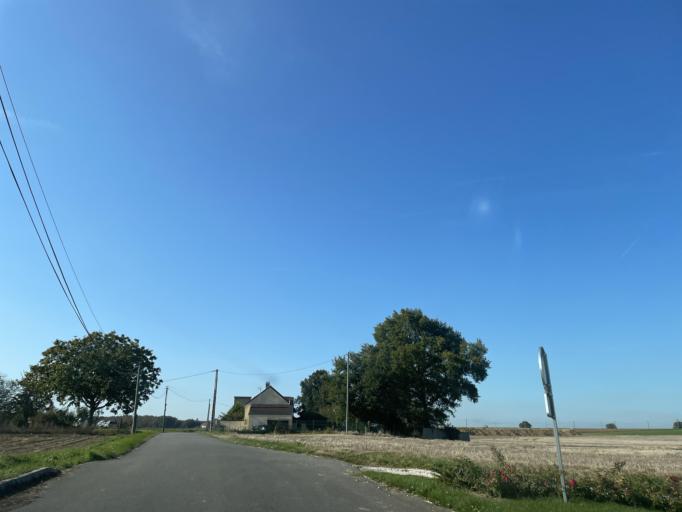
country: FR
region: Ile-de-France
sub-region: Departement de Seine-et-Marne
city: Chailly-en-Brie
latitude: 48.7840
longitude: 3.1613
